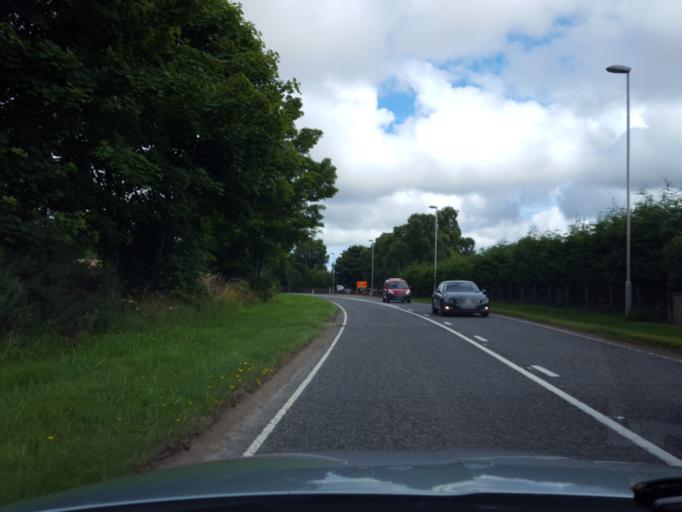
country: GB
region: Scotland
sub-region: Moray
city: Lhanbryd
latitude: 57.5954
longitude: -3.2810
